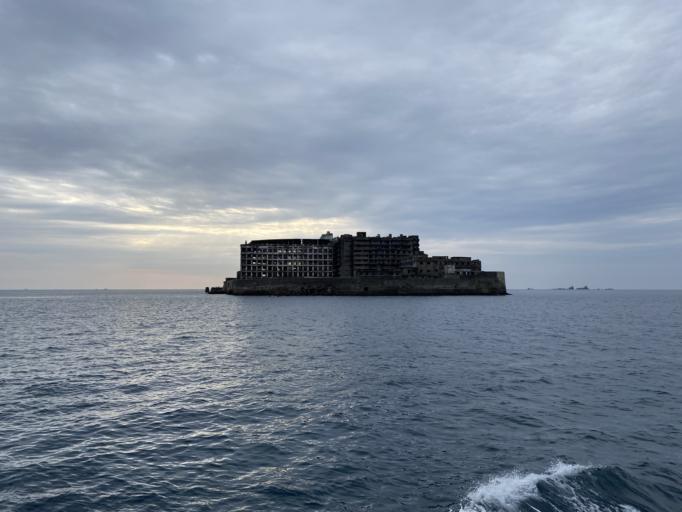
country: JP
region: Nagasaki
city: Nagasaki-shi
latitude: 32.6311
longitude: 129.7414
